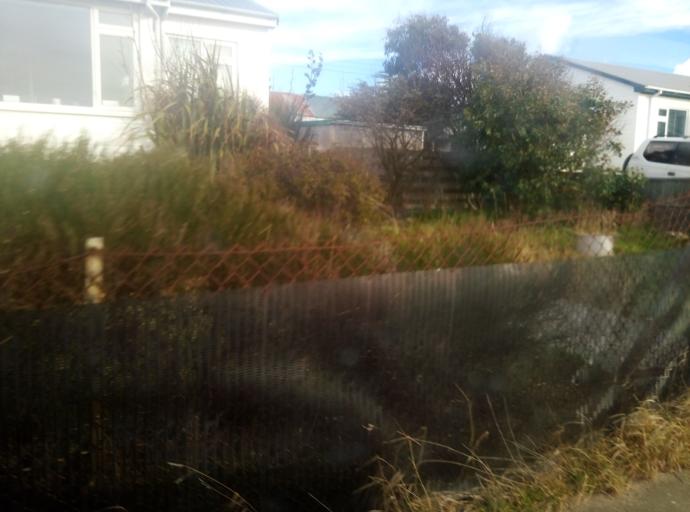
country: FK
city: Stanley
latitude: -51.6903
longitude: -57.8851
